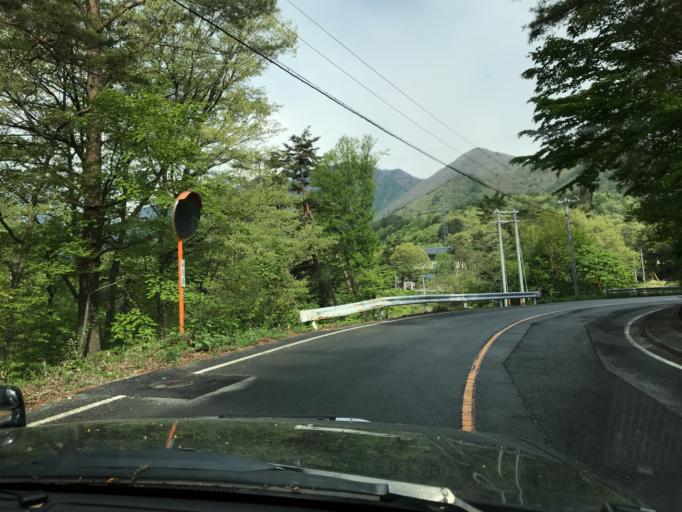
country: JP
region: Nagano
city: Omachi
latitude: 36.5133
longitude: 137.7962
